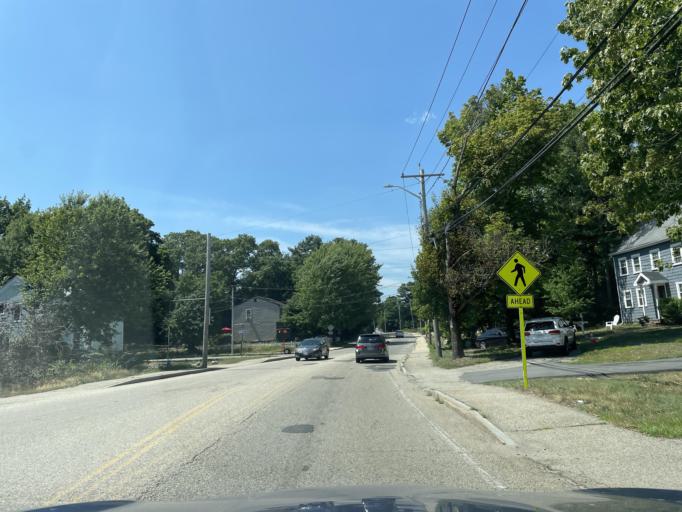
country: US
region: Massachusetts
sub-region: Norfolk County
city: Randolph
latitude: 42.1556
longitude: -71.0289
